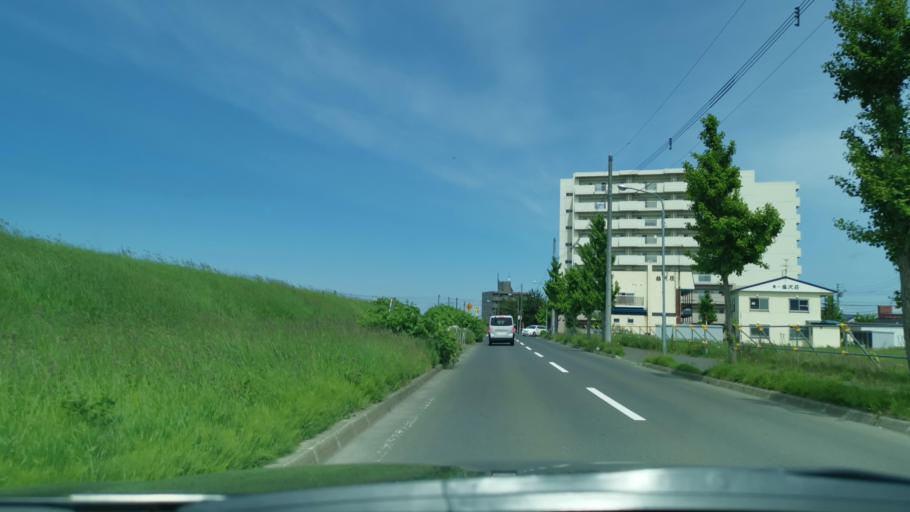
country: JP
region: Hokkaido
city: Sapporo
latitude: 43.0666
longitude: 141.3888
